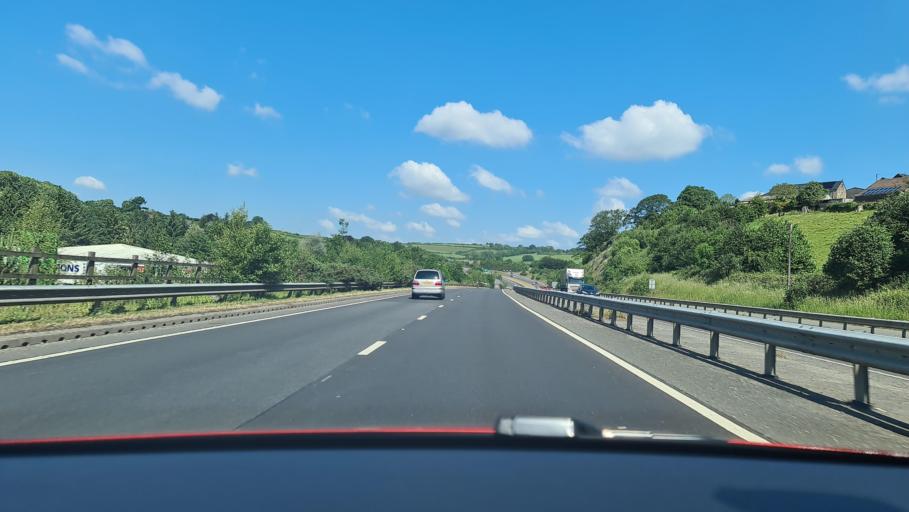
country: GB
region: England
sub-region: Cornwall
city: Liskeard
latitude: 50.4532
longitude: -4.4875
